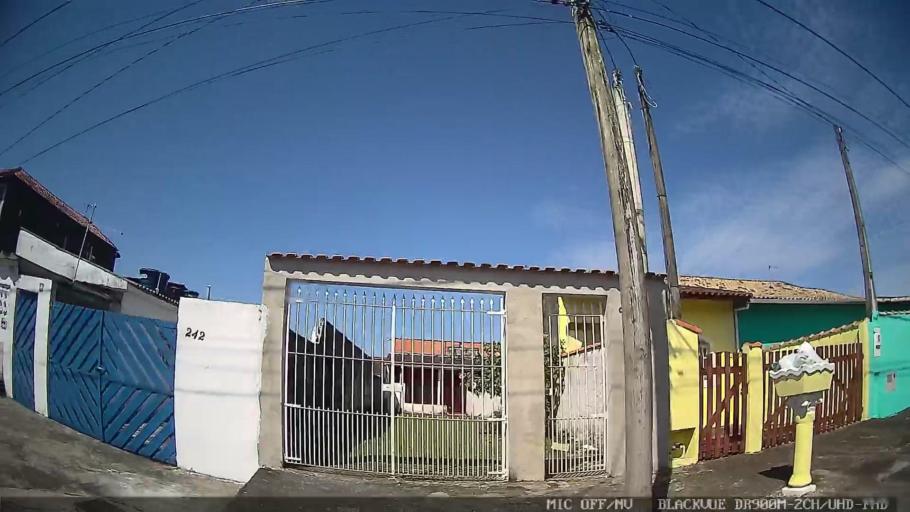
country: BR
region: Sao Paulo
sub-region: Itanhaem
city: Itanhaem
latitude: -24.1491
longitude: -46.7325
